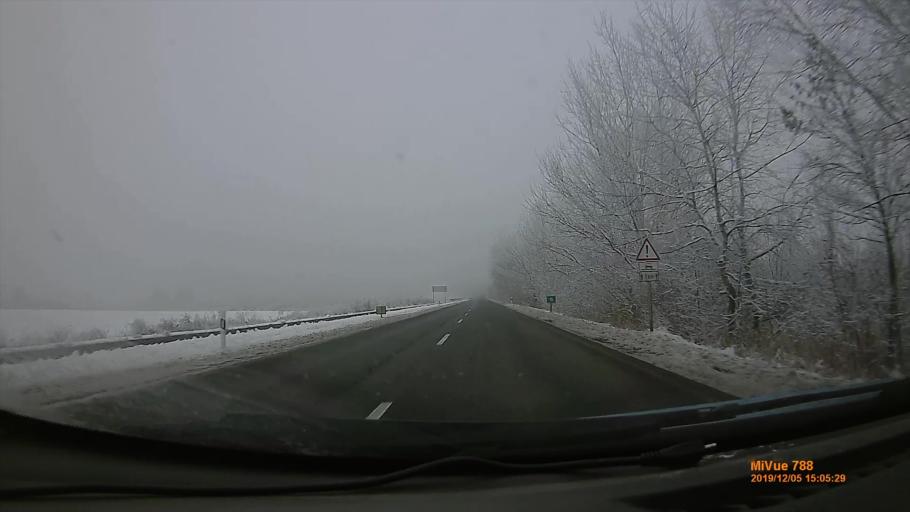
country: HU
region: Szabolcs-Szatmar-Bereg
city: Tiszanagyfalu
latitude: 48.1104
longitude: 21.4864
